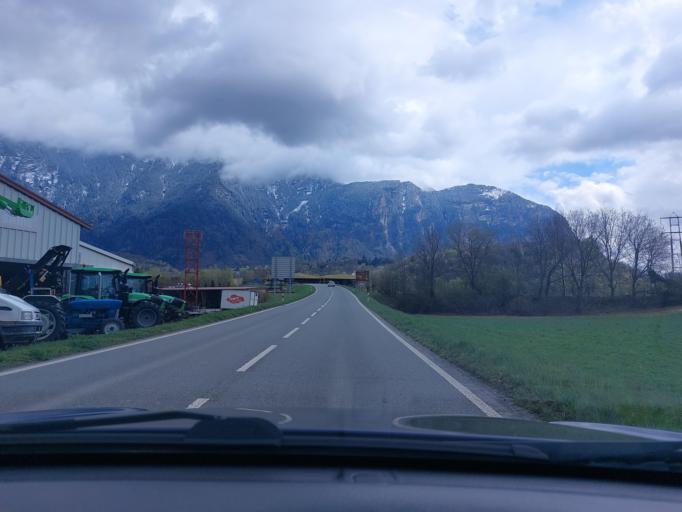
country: CH
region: Vaud
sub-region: Aigle District
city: Bex
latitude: 46.2448
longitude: 6.9977
